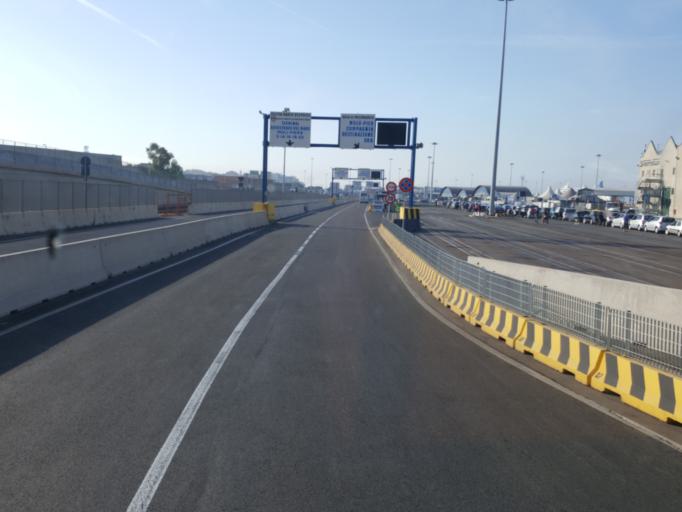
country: IT
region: Latium
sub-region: Citta metropolitana di Roma Capitale
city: Civitavecchia
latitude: 42.1028
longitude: 11.7818
